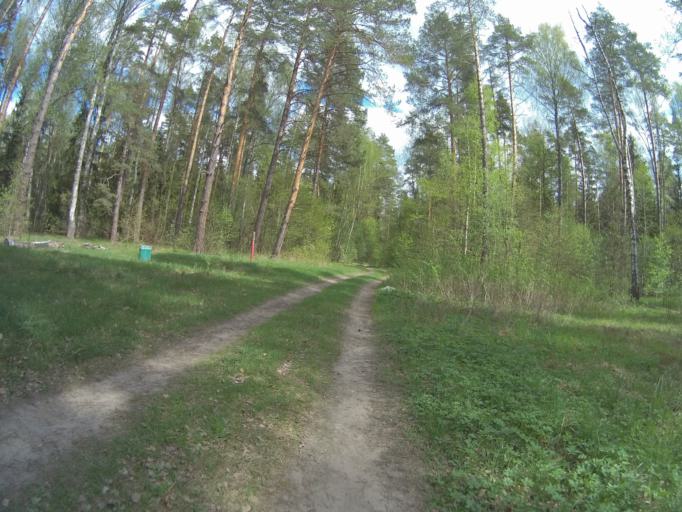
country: RU
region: Vladimir
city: Orgtrud
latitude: 56.1234
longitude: 40.6564
